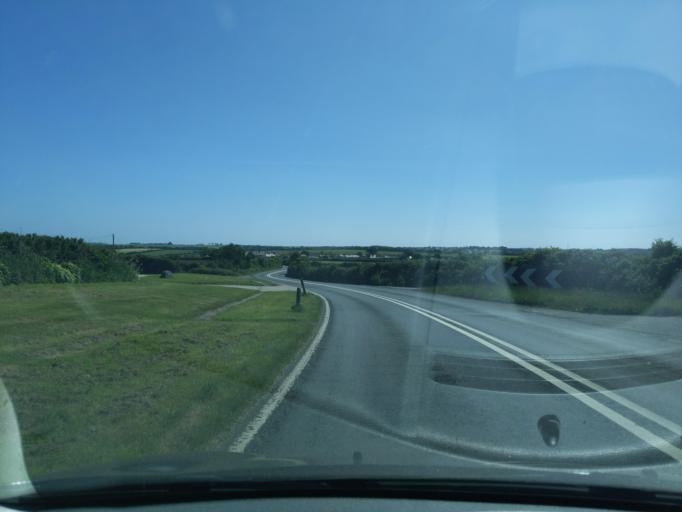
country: GB
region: England
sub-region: Cornwall
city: Wendron
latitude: 50.1171
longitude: -5.2436
